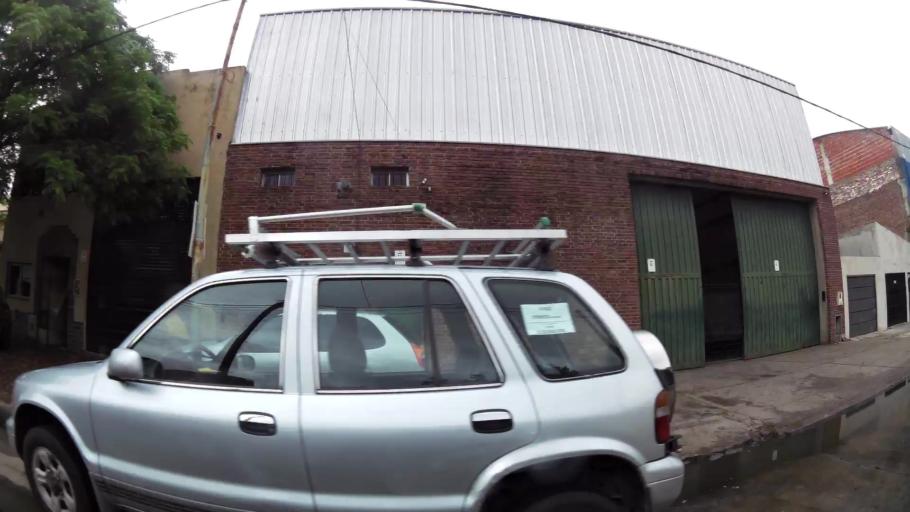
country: AR
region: Buenos Aires
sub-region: Partido de Lanus
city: Lanus
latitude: -34.7276
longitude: -58.3828
